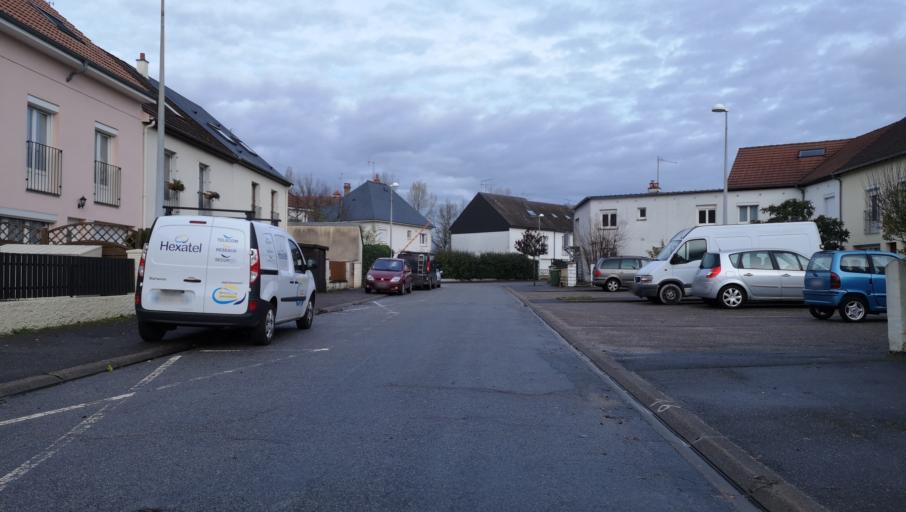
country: FR
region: Centre
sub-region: Departement du Loiret
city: Saint-Jean-de-Braye
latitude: 47.9210
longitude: 1.9635
